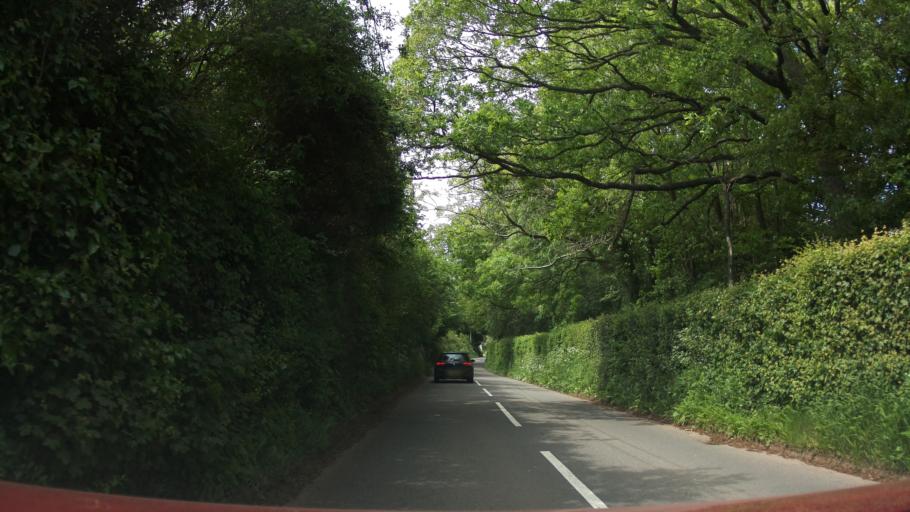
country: GB
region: England
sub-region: Herefordshire
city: Llanrothal
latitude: 51.8610
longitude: -2.8121
